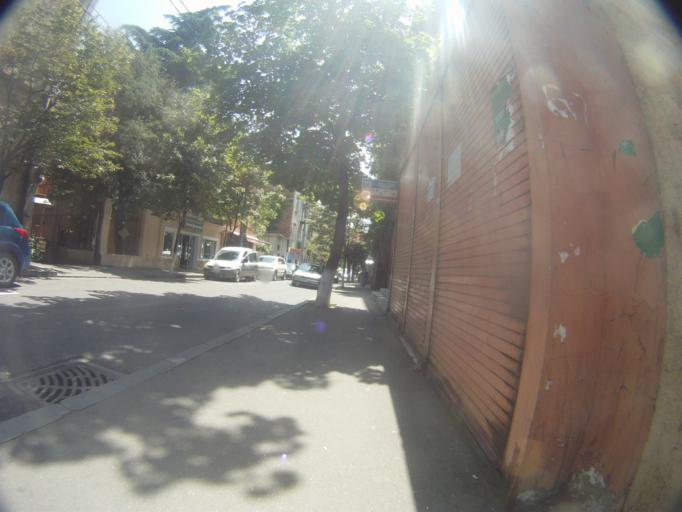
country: GE
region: T'bilisi
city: Tbilisi
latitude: 41.7066
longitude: 44.7893
